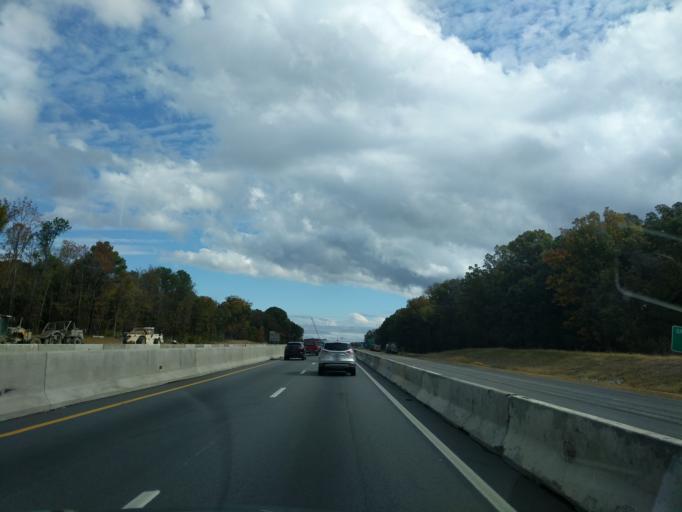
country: US
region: North Carolina
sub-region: Cabarrus County
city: Kannapolis
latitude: 35.4420
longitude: -80.6239
